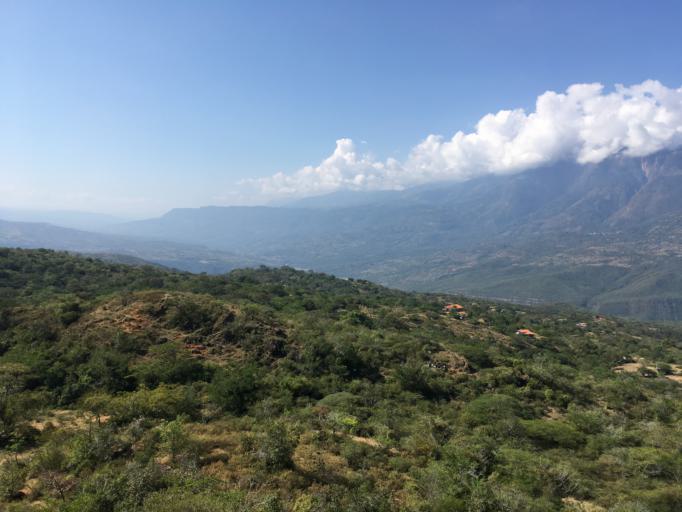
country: CO
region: Santander
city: Barichara
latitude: 6.6681
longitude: -73.2350
